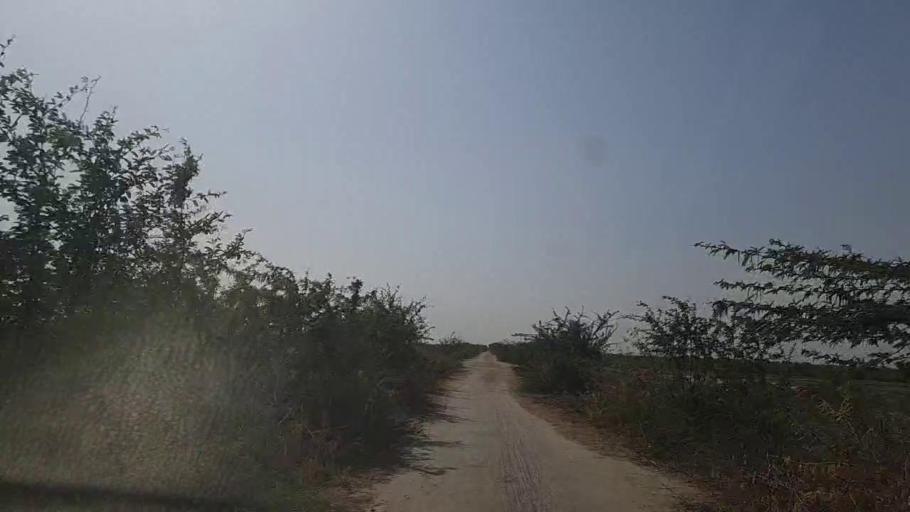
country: PK
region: Sindh
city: Kadhan
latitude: 24.5689
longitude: 69.2849
